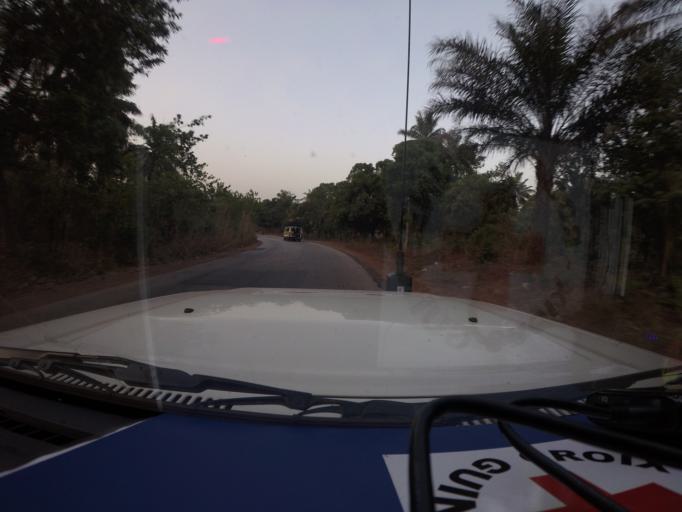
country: GN
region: Kindia
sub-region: Kindia
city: Kindia
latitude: 9.8968
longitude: -13.0466
